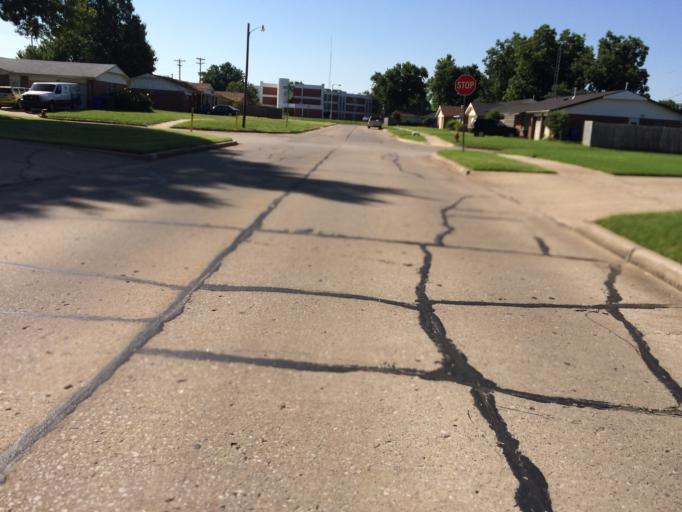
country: US
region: Oklahoma
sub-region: Cleveland County
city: Norman
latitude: 35.2283
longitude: -97.4615
